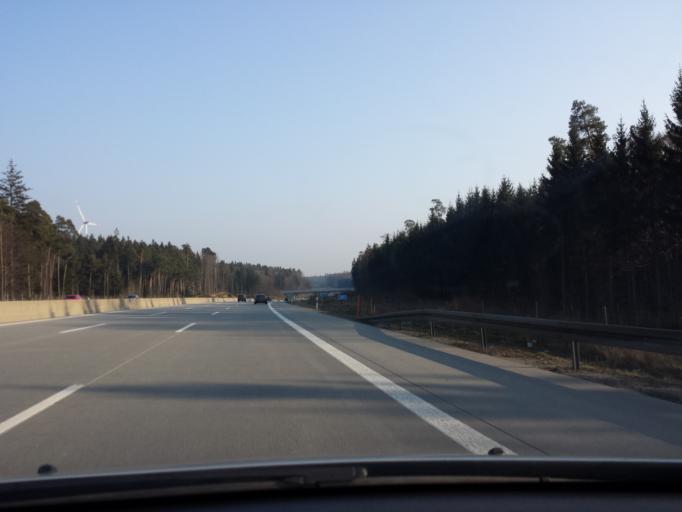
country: DE
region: Bavaria
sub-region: Swabia
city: Adelzhausen
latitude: 48.3398
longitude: 11.1558
